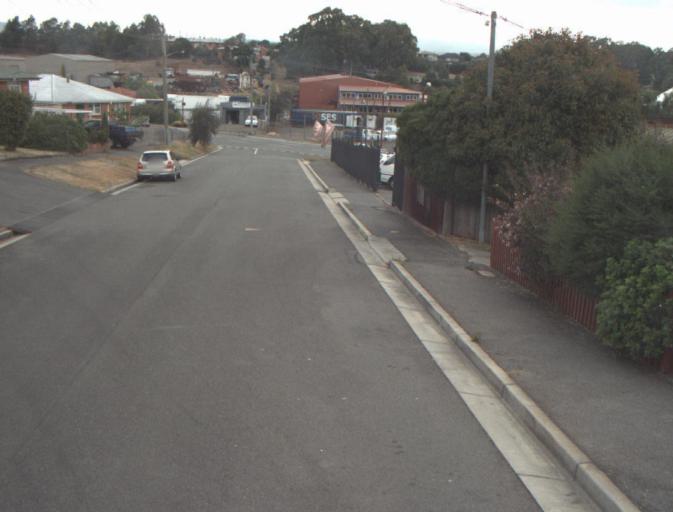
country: AU
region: Tasmania
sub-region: Launceston
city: Summerhill
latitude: -41.4834
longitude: 147.1665
